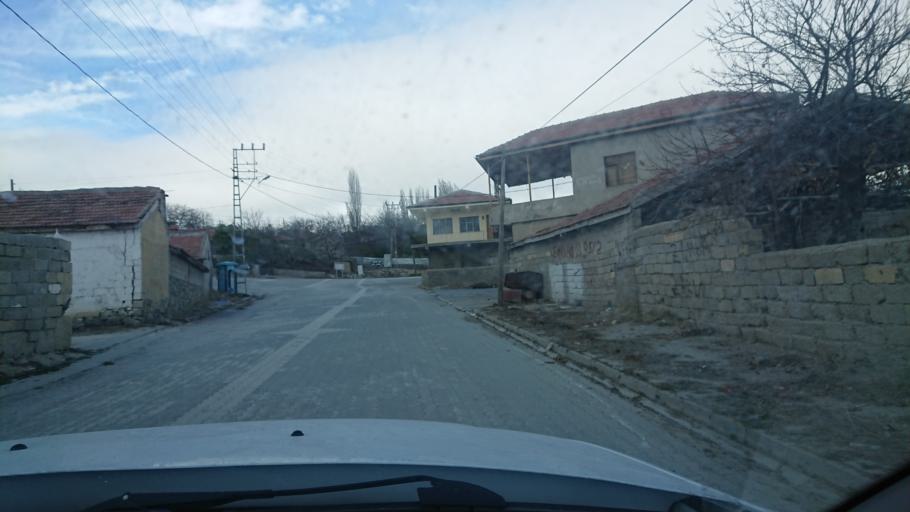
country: TR
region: Aksaray
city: Ortakoy
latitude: 38.7583
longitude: 34.0109
